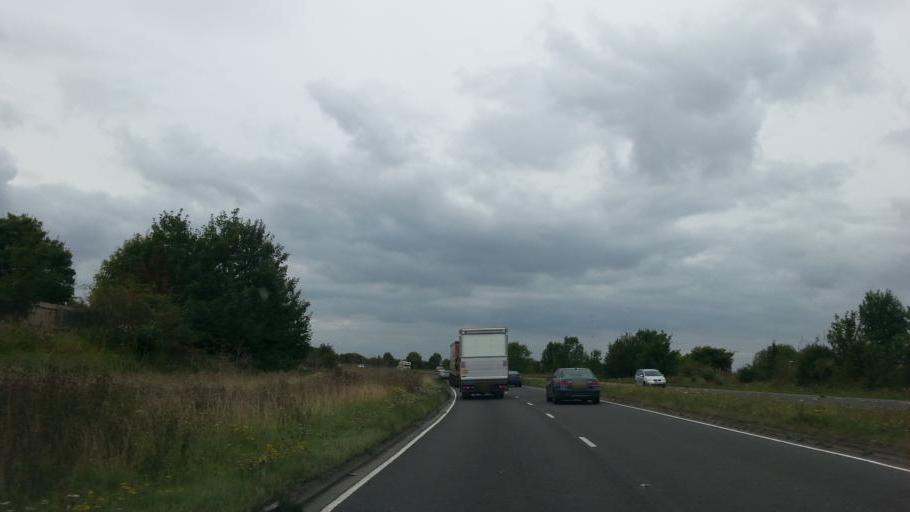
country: GB
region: England
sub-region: Hertfordshire
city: Royston
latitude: 52.0630
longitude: -0.0173
